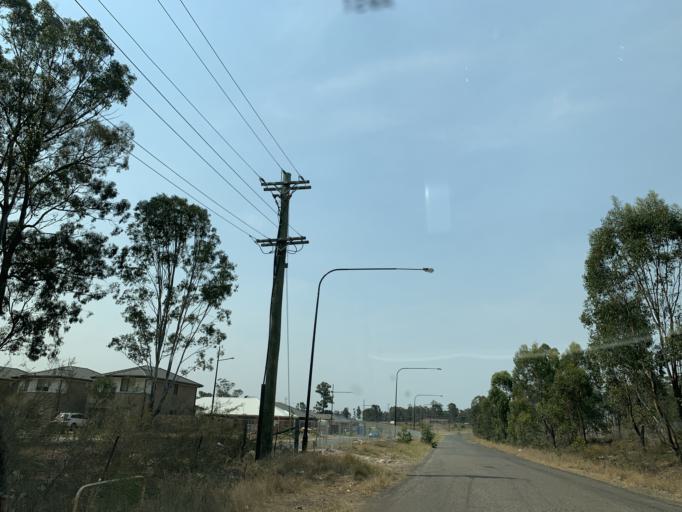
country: AU
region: New South Wales
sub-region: Blacktown
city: Blackett
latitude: -33.7141
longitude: 150.8206
